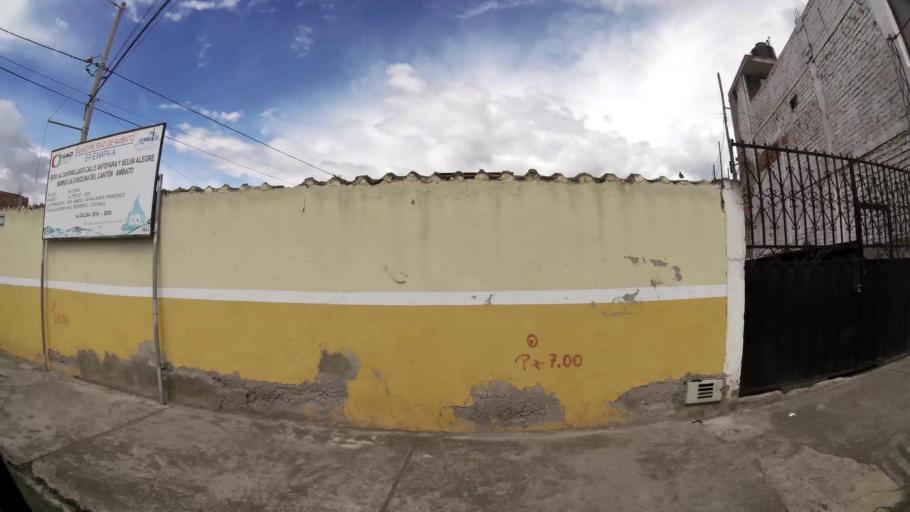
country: EC
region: Tungurahua
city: Ambato
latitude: -1.2598
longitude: -78.6207
